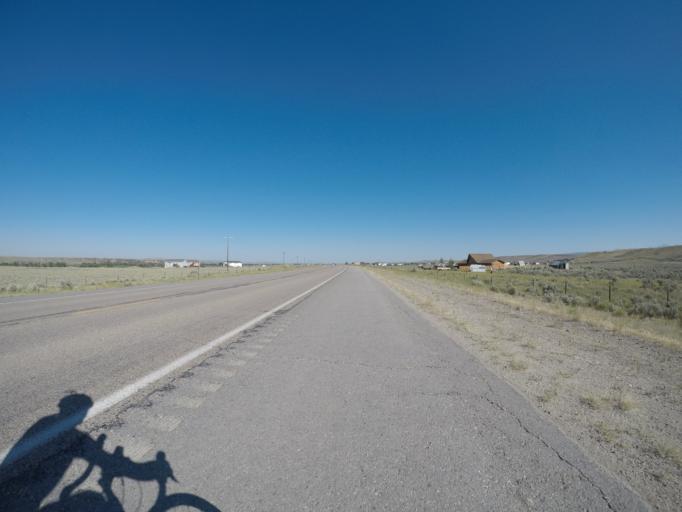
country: US
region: Wyoming
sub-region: Sublette County
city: Pinedale
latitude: 42.7616
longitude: -109.7353
